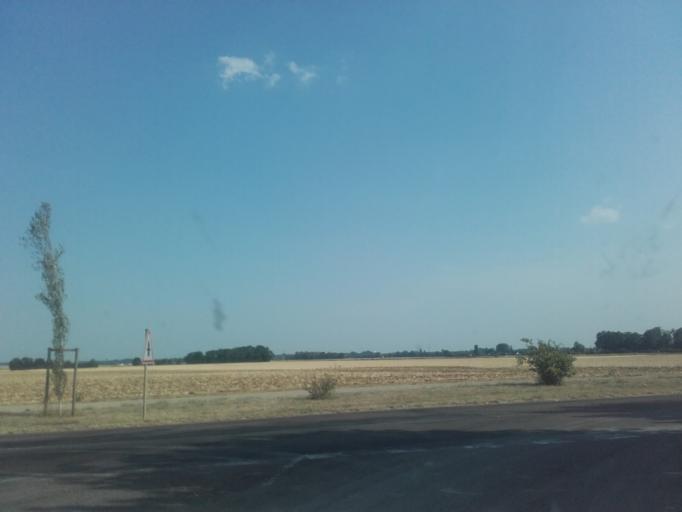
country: FR
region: Bourgogne
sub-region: Departement de la Cote-d'Or
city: Beaune
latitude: 47.0213
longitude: 4.8753
